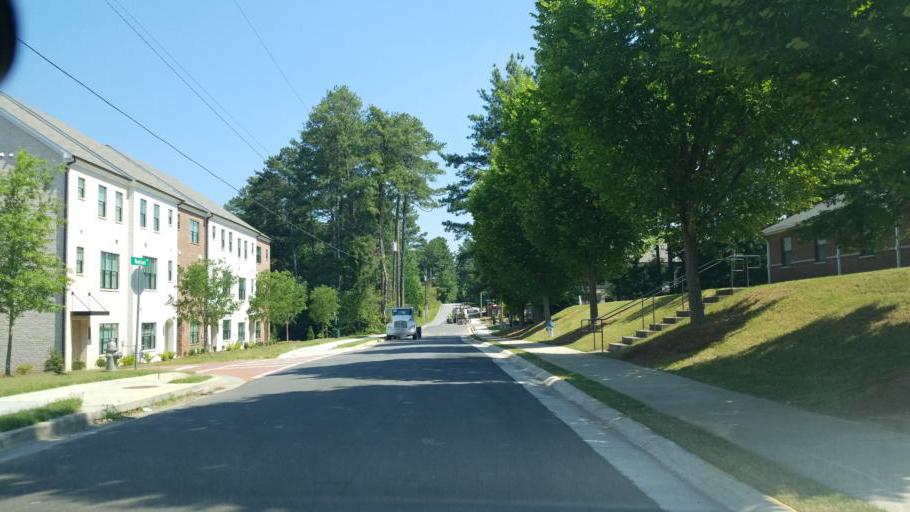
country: US
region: Georgia
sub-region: Cobb County
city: Vinings
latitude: 33.8846
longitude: -84.4793
